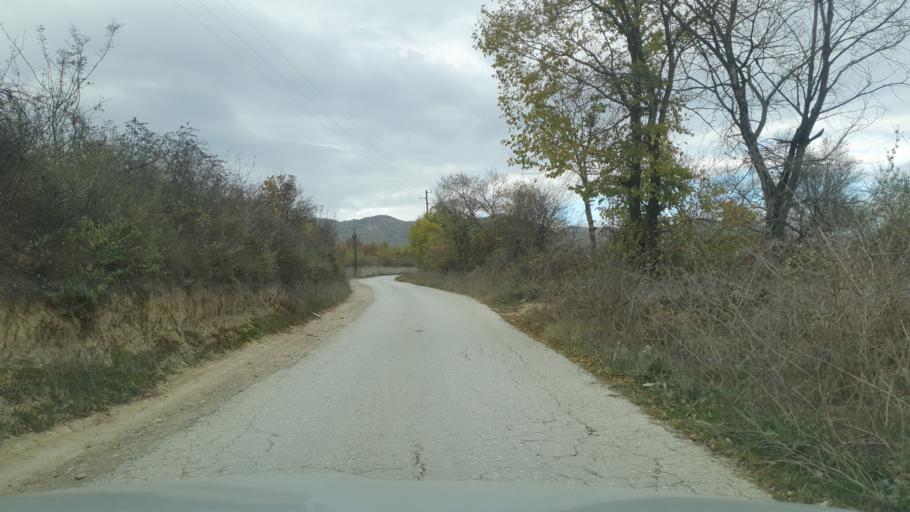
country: MK
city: Kondovo
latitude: 42.0377
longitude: 21.2810
